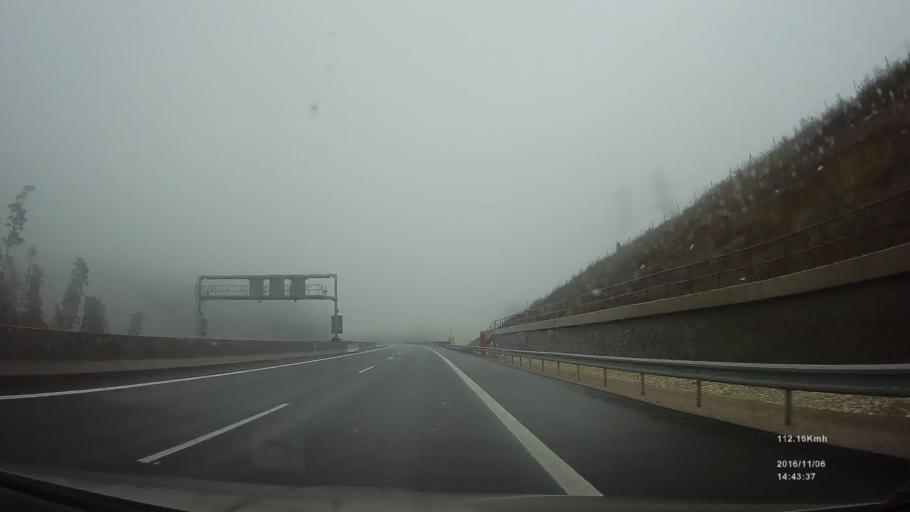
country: SK
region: Presovsky
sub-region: Okres Presov
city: Levoca
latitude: 49.0068
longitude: 20.6316
